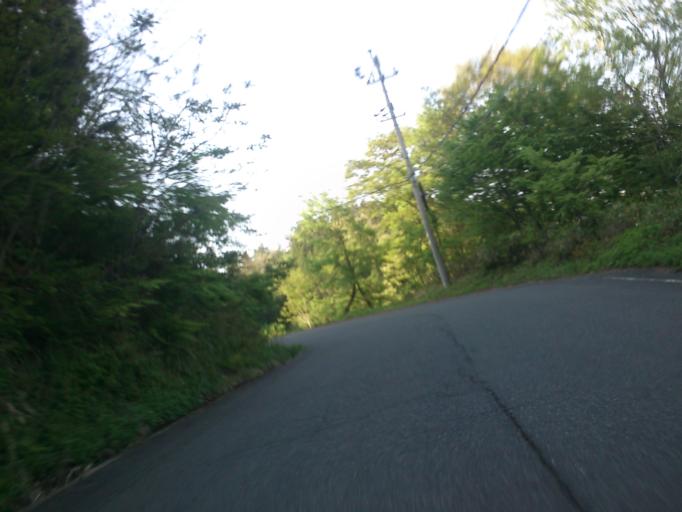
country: JP
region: Kyoto
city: Miyazu
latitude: 35.7162
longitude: 135.1941
